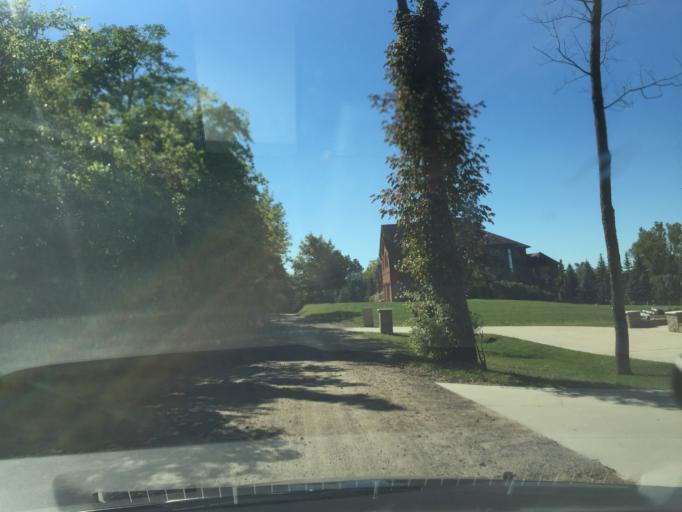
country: US
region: Michigan
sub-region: Oakland County
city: Sylvan Lake
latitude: 42.6057
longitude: -83.3079
